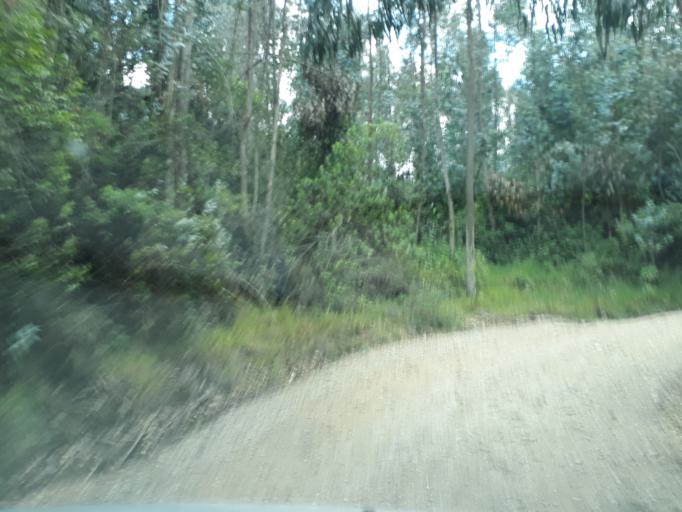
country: CO
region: Cundinamarca
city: Lenguazaque
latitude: 5.2702
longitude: -73.6910
